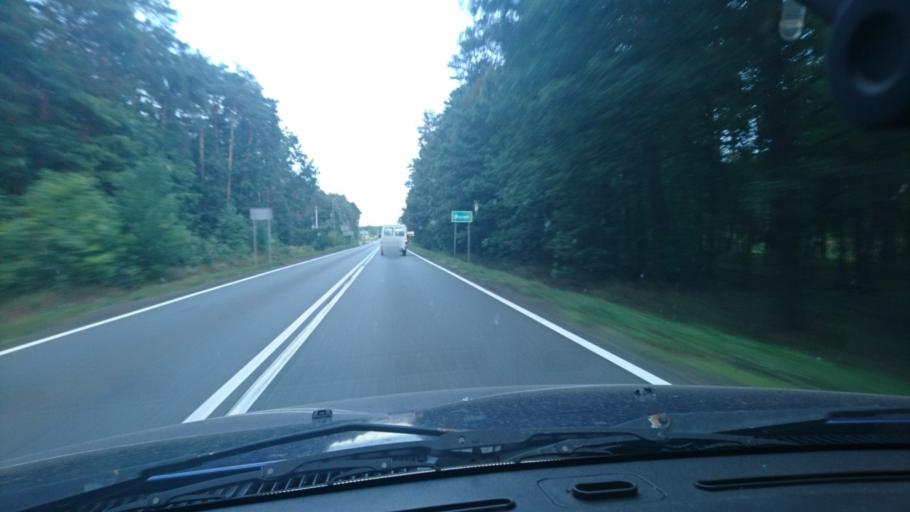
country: PL
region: Silesian Voivodeship
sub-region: Powiat tarnogorski
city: Tworog
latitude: 50.5232
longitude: 18.7215
